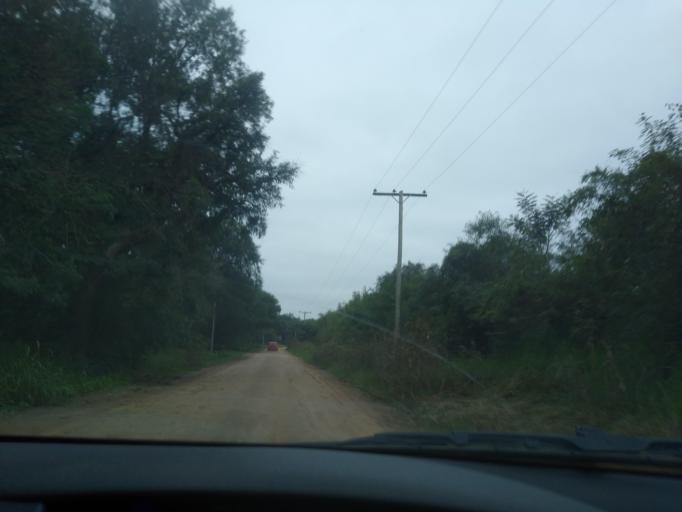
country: AR
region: Chaco
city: Colonia Benitez
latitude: -27.3356
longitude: -58.9609
